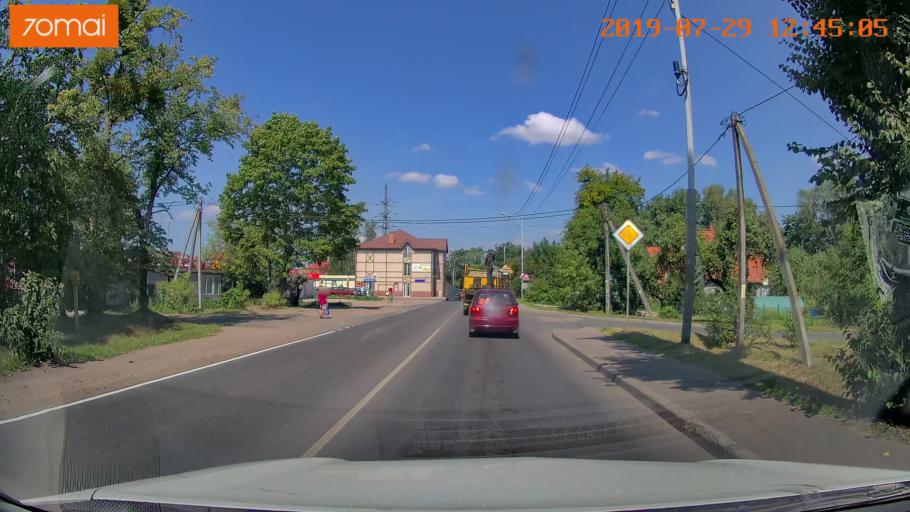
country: RU
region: Kaliningrad
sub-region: Gorod Kaliningrad
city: Kaliningrad
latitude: 54.6811
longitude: 20.5358
